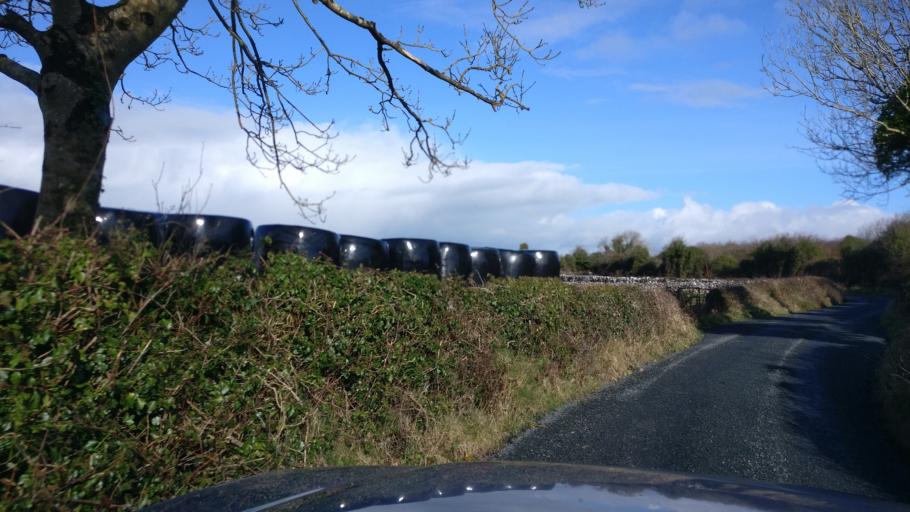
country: IE
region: Connaught
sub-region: County Galway
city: Athenry
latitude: 53.2349
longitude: -8.7738
